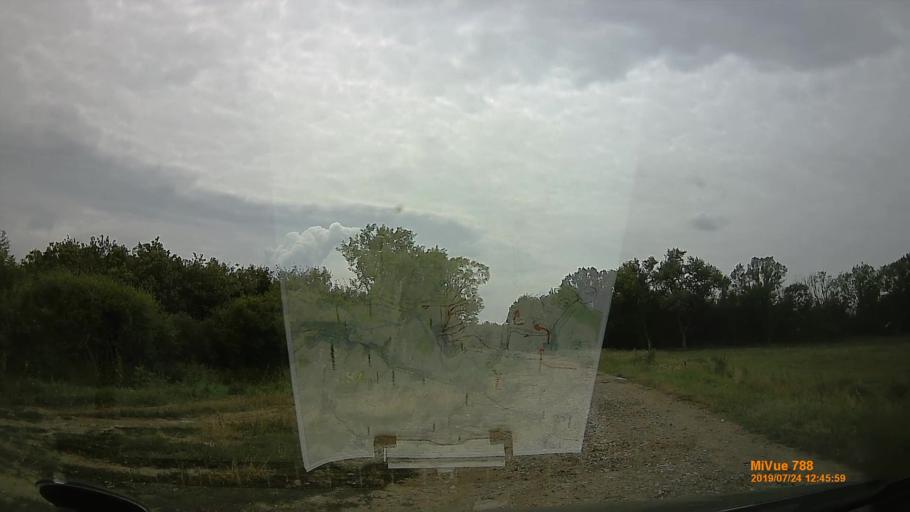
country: HU
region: Szabolcs-Szatmar-Bereg
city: Aranyosapati
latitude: 48.1977
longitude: 22.3209
